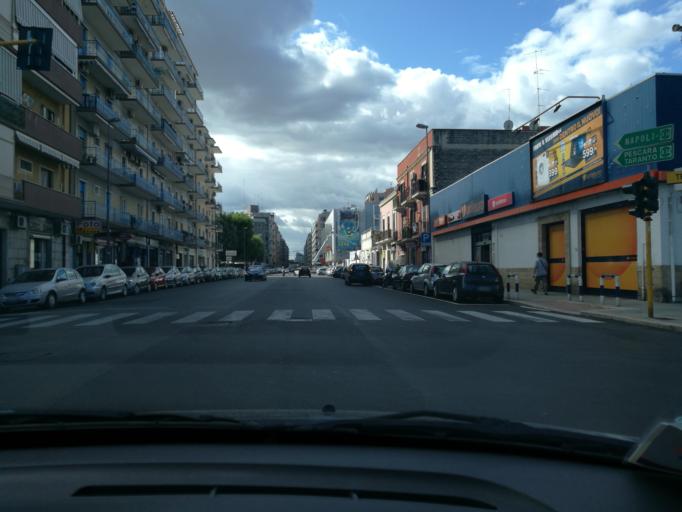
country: IT
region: Apulia
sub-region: Provincia di Bari
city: Bari
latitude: 41.1252
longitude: 16.8517
